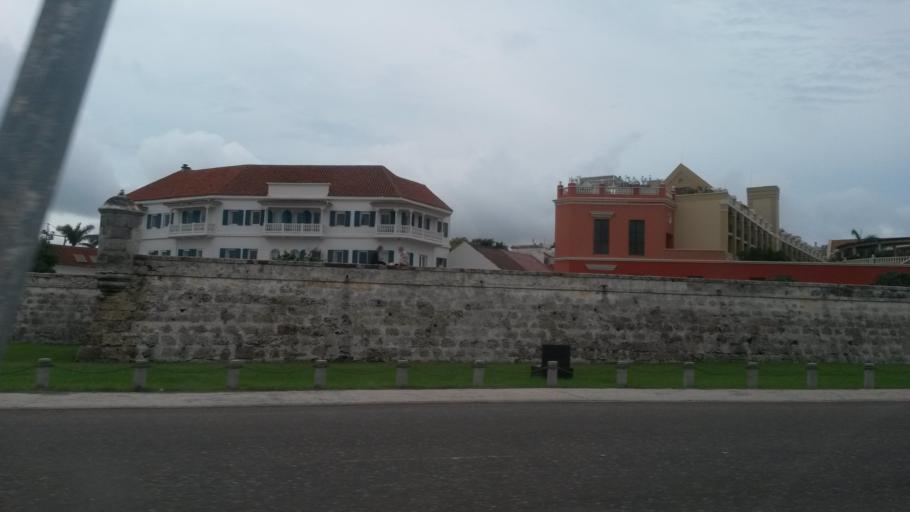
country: CO
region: Bolivar
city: Cartagena
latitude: 10.4300
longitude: -75.5476
